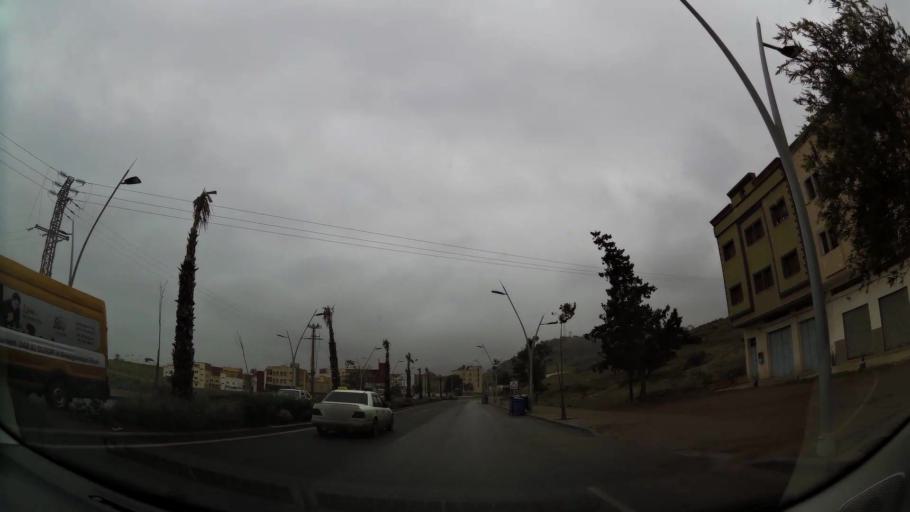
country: MA
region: Oriental
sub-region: Nador
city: Nador
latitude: 35.1925
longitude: -2.9312
